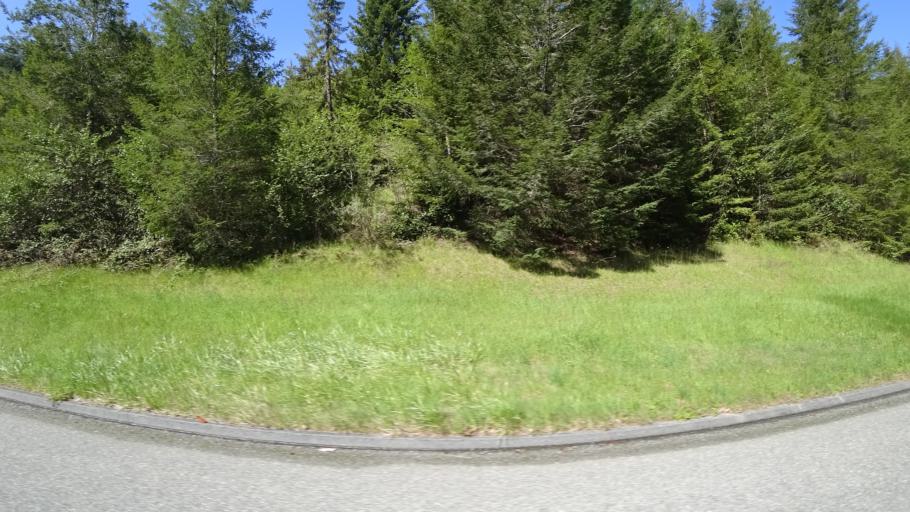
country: US
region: California
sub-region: Humboldt County
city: Westhaven-Moonstone
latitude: 41.4011
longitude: -123.9929
